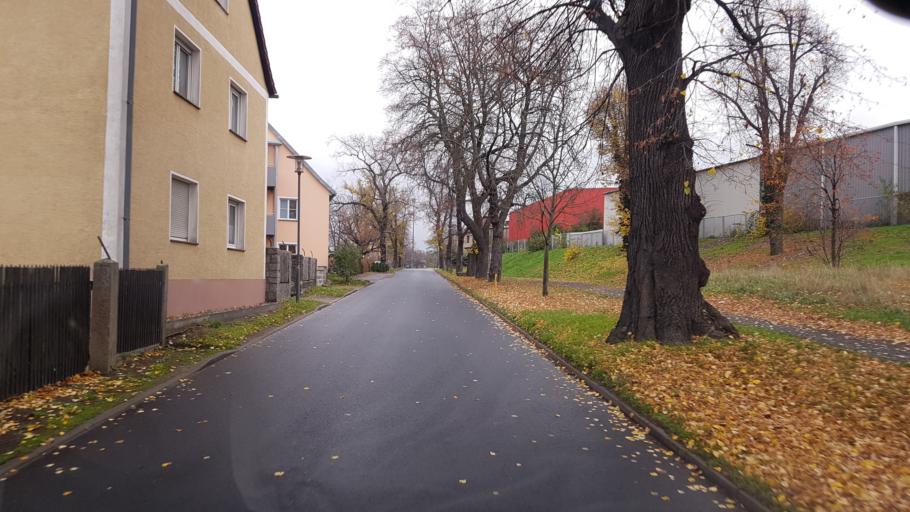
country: DE
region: Brandenburg
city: Ortrand
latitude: 51.3736
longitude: 13.7600
